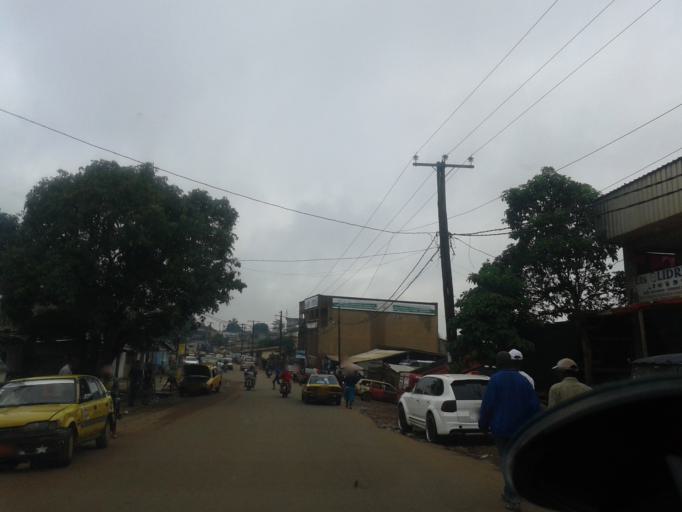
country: CM
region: Centre
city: Yaounde
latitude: 3.9076
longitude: 11.5296
